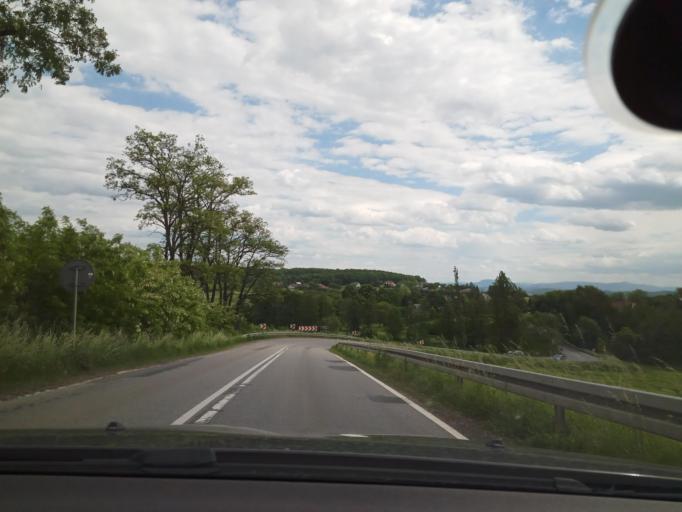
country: PL
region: Lesser Poland Voivodeship
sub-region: Powiat wielicki
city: Trabki
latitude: 49.9488
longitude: 20.1657
